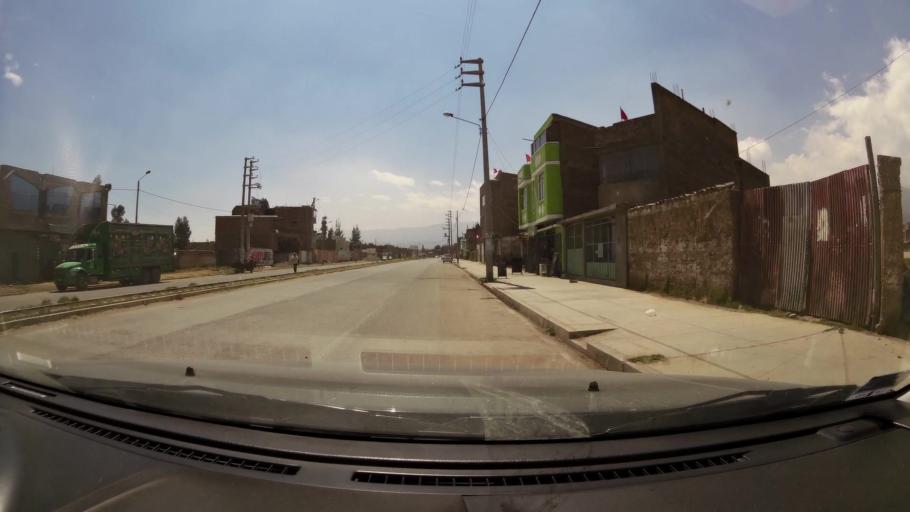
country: PE
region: Junin
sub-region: Provincia de Huancayo
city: El Tambo
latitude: -12.0887
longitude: -75.2145
